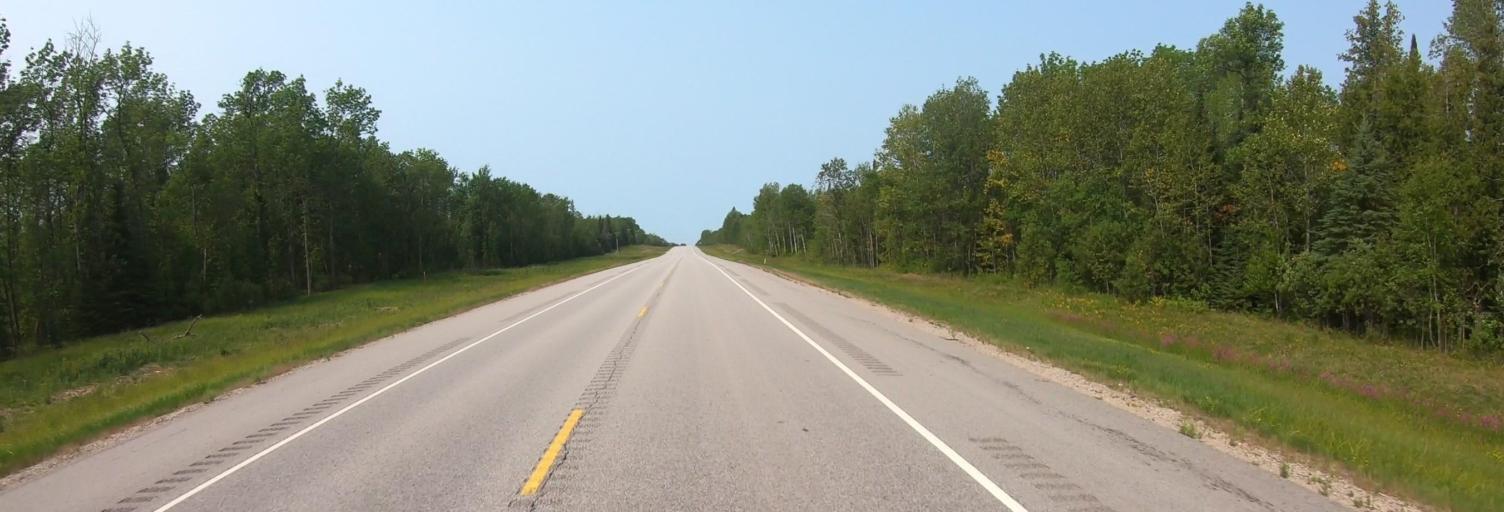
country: CA
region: Ontario
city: Fort Frances
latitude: 48.4086
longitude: -93.0570
